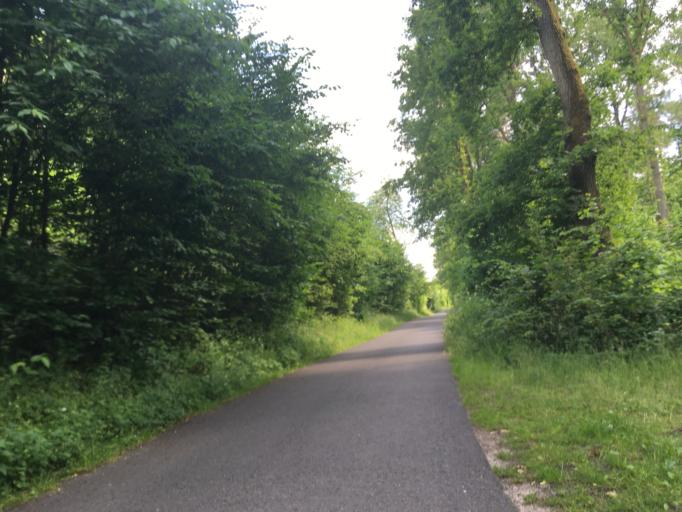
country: DE
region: Brandenburg
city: Waldsieversdorf
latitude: 52.5388
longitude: 14.0870
